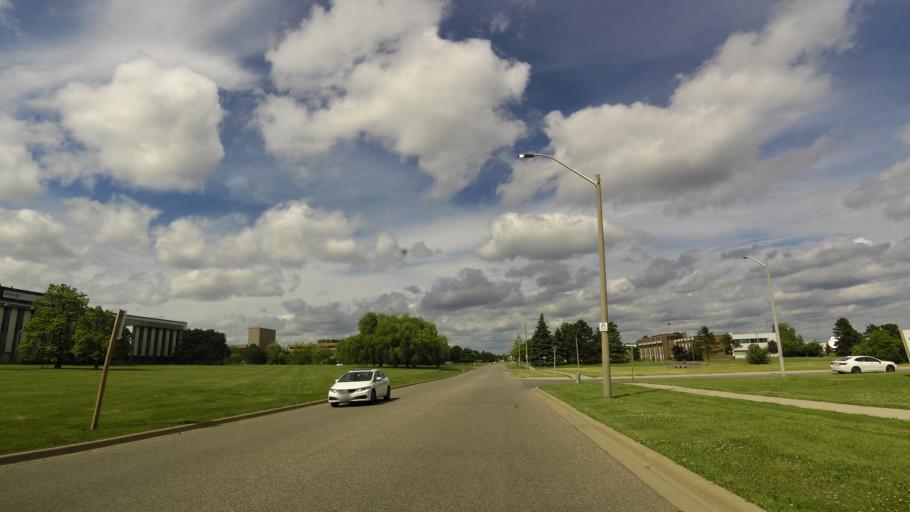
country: CA
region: Ontario
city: Mississauga
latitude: 43.5181
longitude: -79.6611
